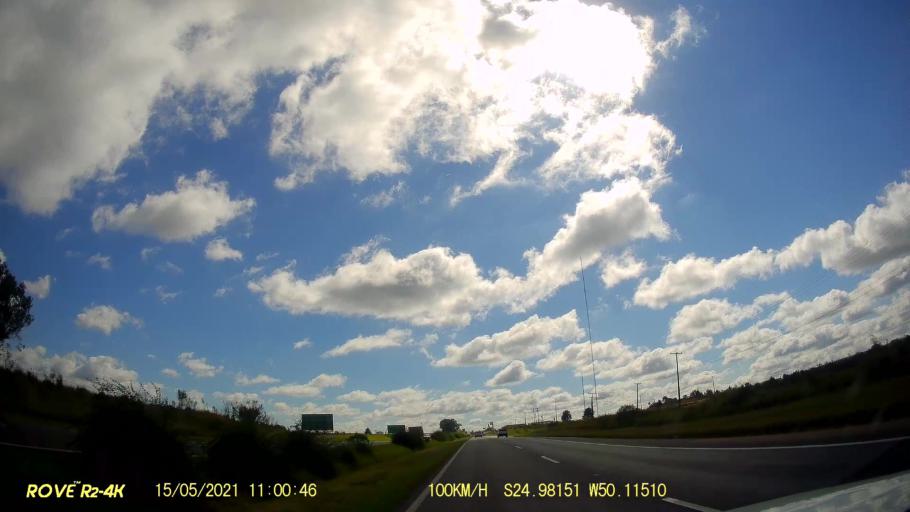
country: BR
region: Parana
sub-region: Carambei
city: Carambei
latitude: -24.9817
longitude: -50.1151
